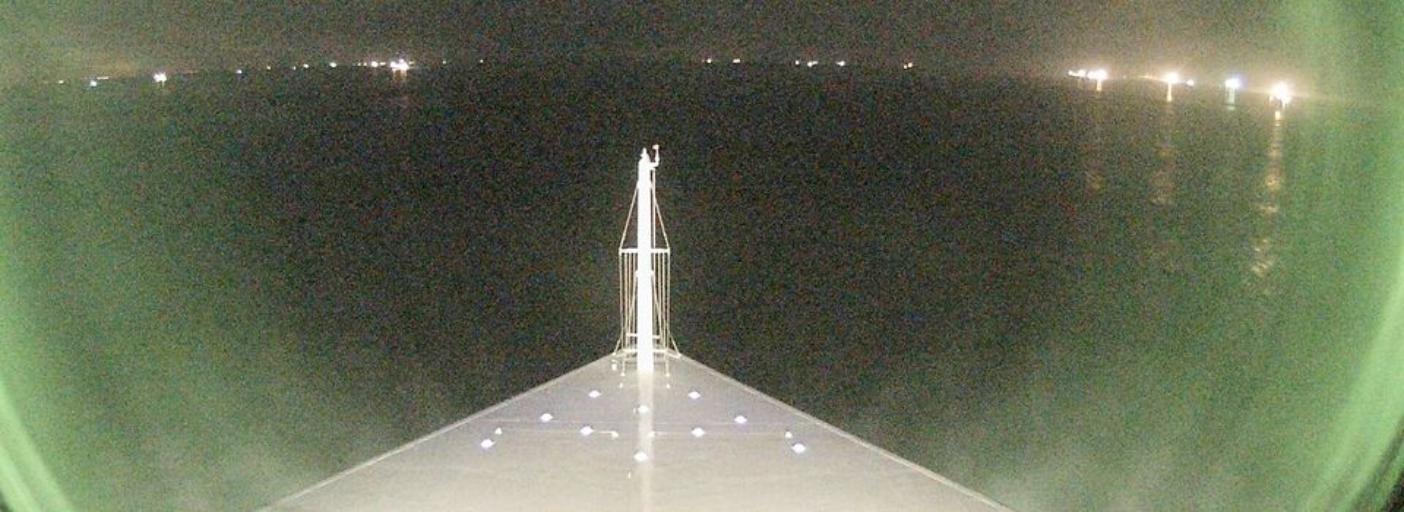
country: DE
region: Schleswig-Holstein
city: Helgoland
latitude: 54.0080
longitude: 8.1738
